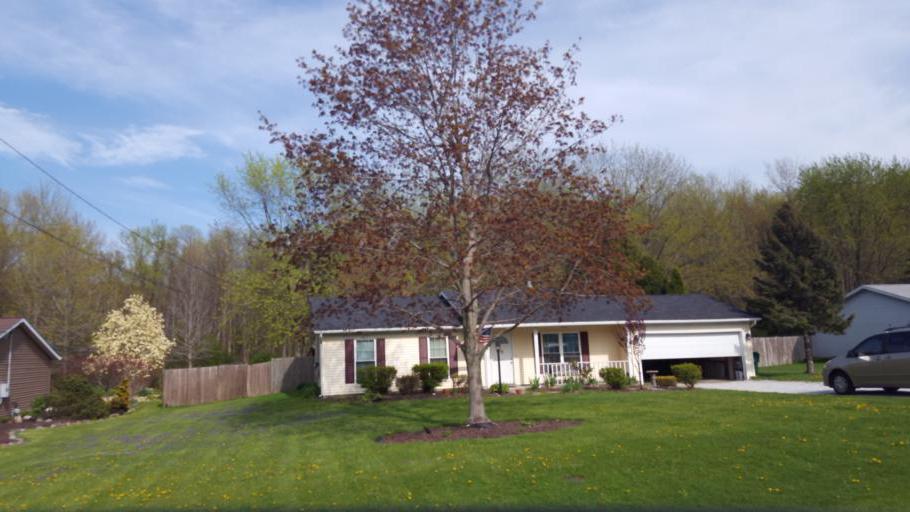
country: US
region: Ohio
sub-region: Lake County
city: North Madison
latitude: 41.8284
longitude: -81.0618
